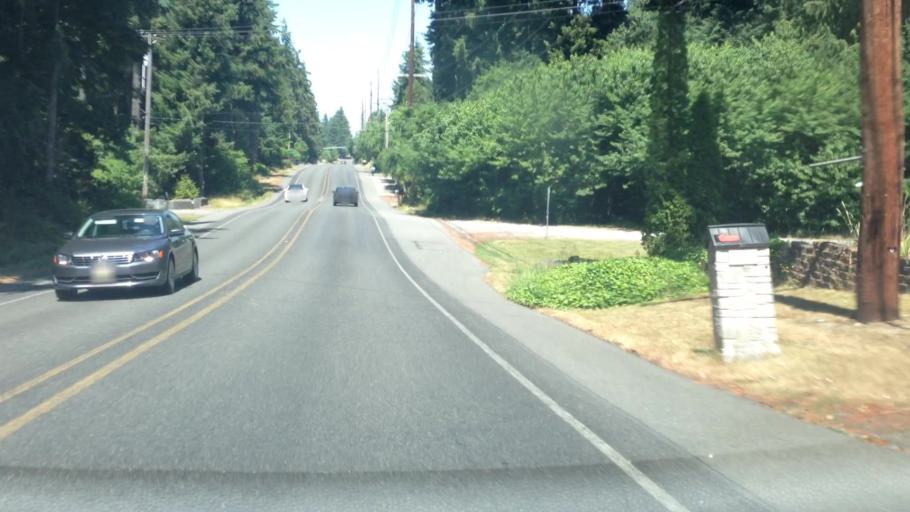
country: US
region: Washington
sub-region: Pierce County
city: Puyallup
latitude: 47.1514
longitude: -122.3148
